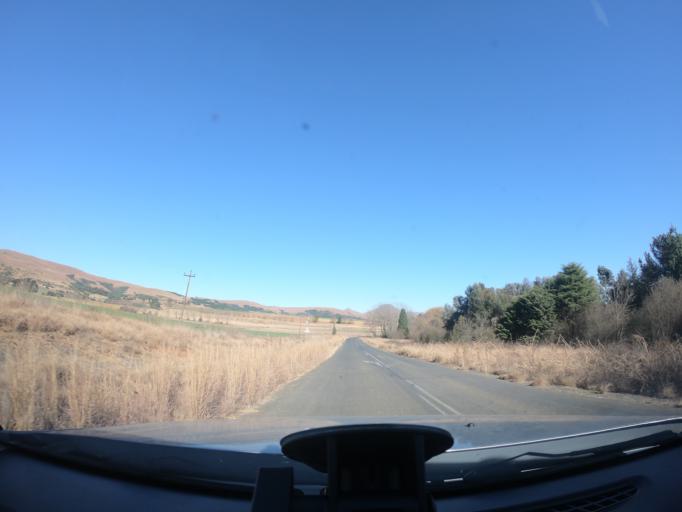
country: ZA
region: KwaZulu-Natal
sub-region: uMgungundlovu District Municipality
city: Mooirivier
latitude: -29.3277
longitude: 29.8498
